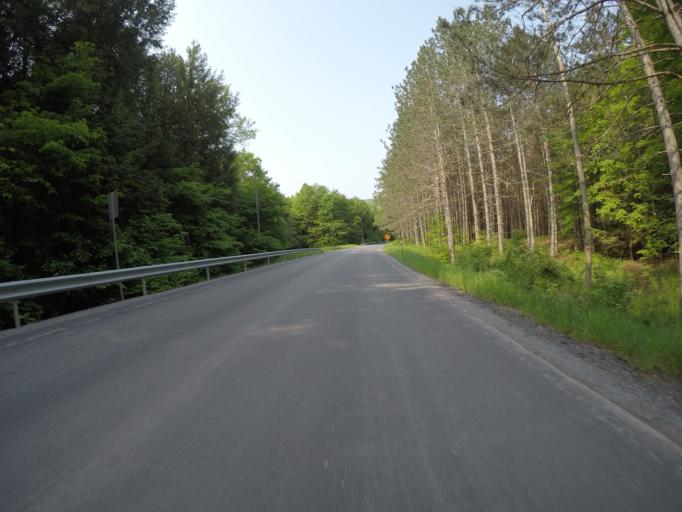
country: US
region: New York
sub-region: Sullivan County
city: Livingston Manor
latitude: 42.1169
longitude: -74.7209
